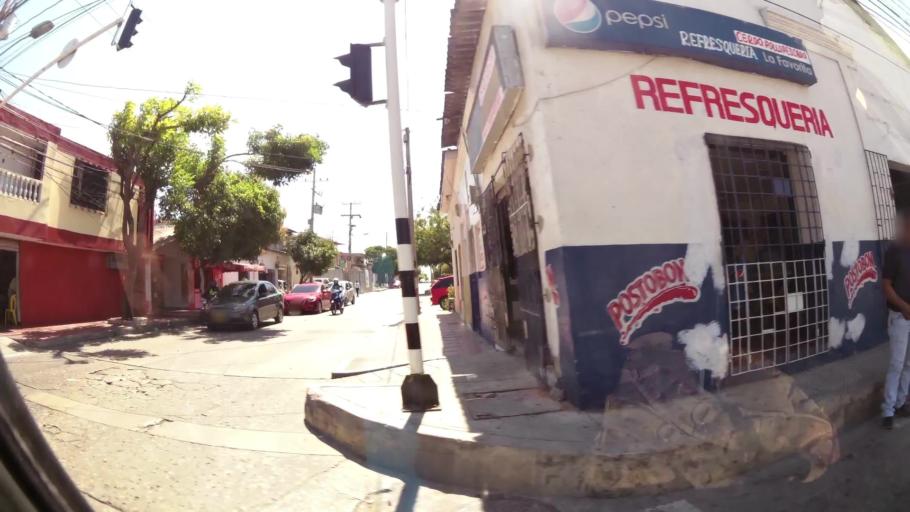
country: CO
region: Atlantico
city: Barranquilla
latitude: 10.9754
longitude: -74.7895
